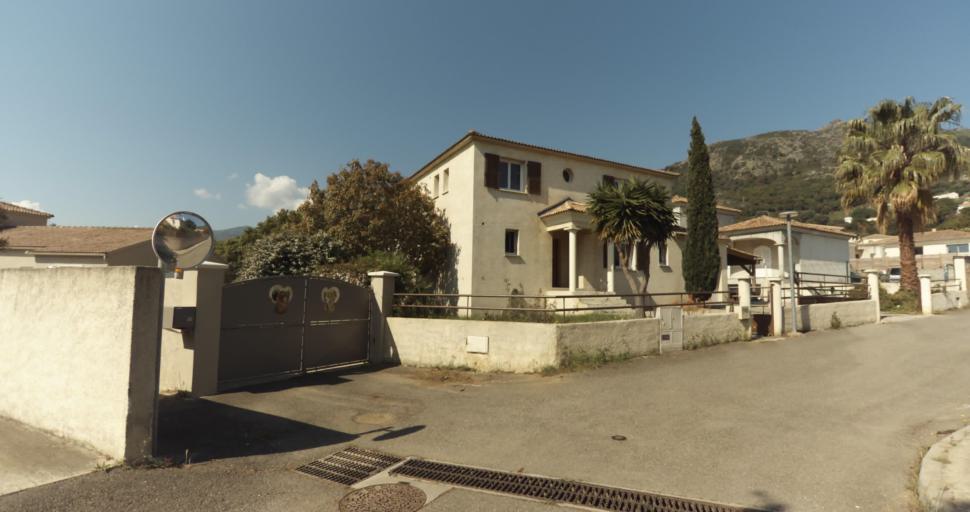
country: FR
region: Corsica
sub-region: Departement de la Haute-Corse
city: Biguglia
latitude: 42.6250
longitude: 9.4268
